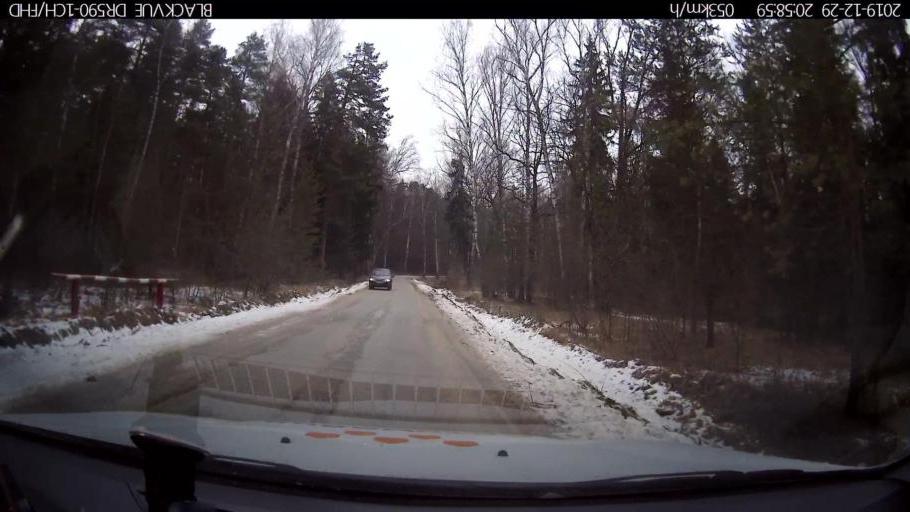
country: RU
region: Nizjnij Novgorod
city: Afonino
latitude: 56.1726
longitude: 43.9875
